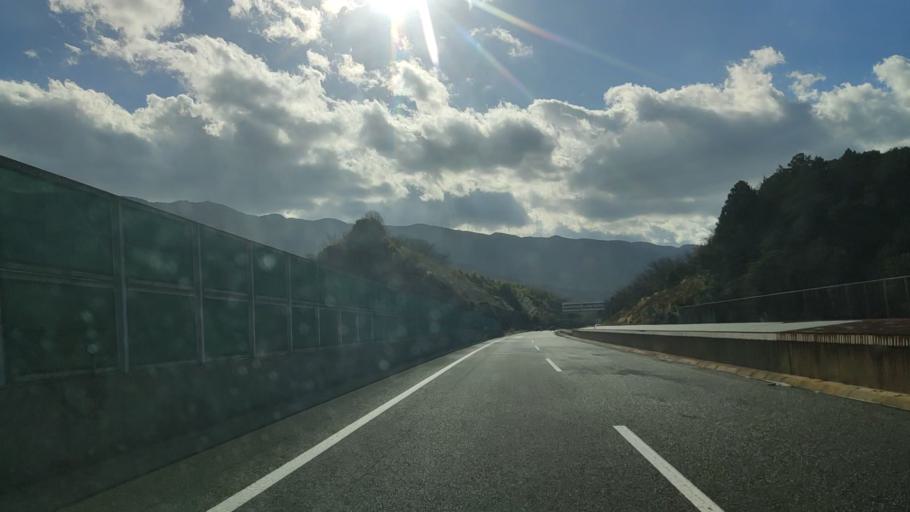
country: JP
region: Ehime
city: Kawanoecho
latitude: 33.9903
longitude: 133.5932
